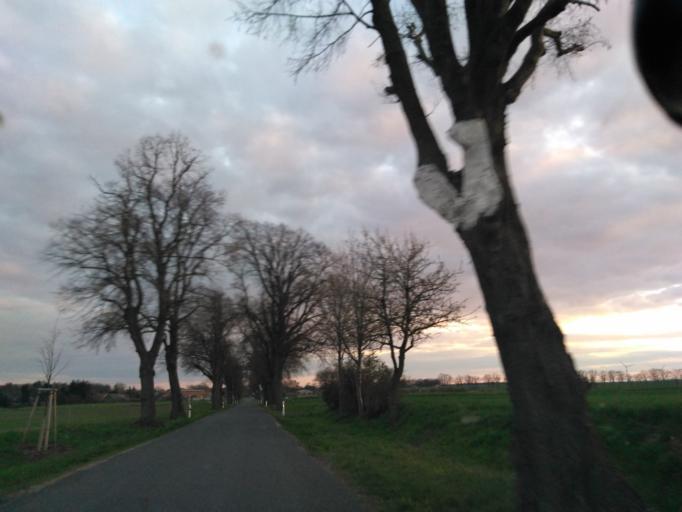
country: DE
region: Brandenburg
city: Protzel
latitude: 52.6570
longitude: 14.0694
